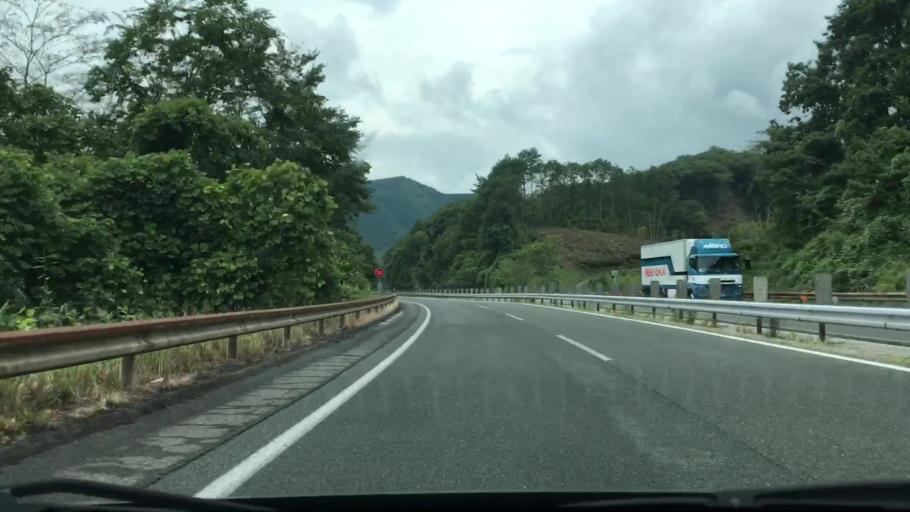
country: JP
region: Okayama
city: Niimi
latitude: 34.9675
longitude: 133.3442
